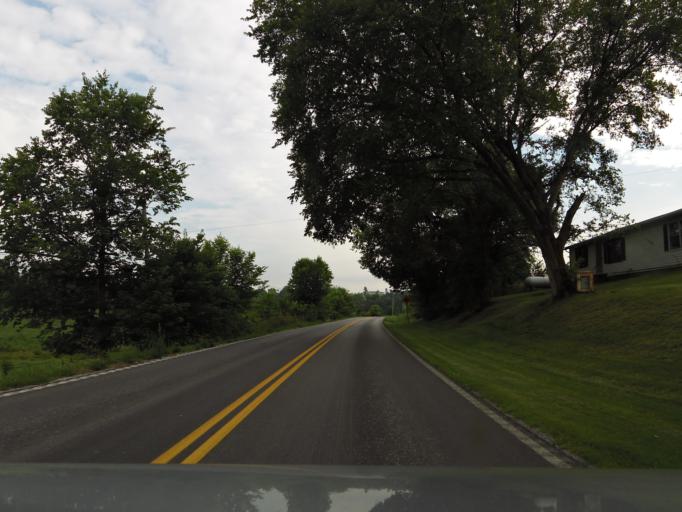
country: US
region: Kentucky
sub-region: Harrison County
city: Cynthiana
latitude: 38.4378
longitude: -84.2487
